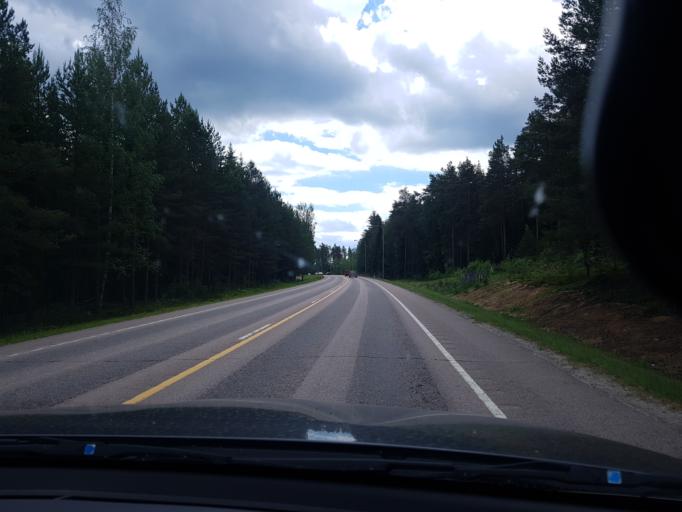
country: FI
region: Pirkanmaa
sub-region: Tampere
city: Paelkaene
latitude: 61.3202
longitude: 24.2850
